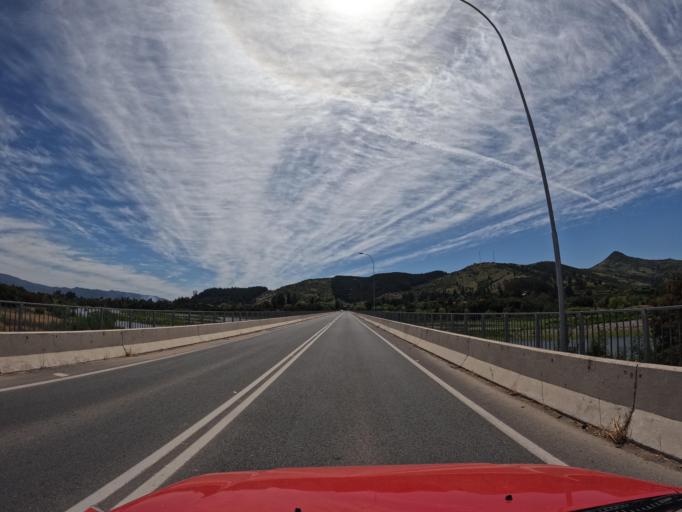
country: CL
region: Maule
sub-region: Provincia de Talca
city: Talca
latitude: -35.0935
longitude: -71.6463
